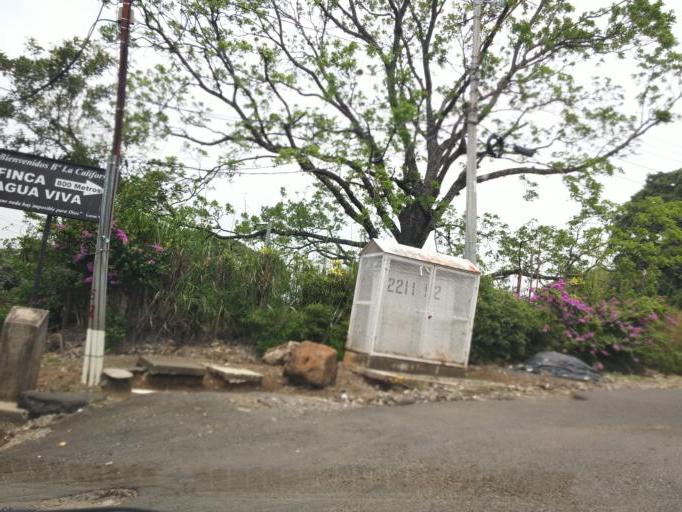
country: CR
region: Heredia
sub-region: Canton de Belen
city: San Antonio
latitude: 9.9925
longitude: -84.1994
